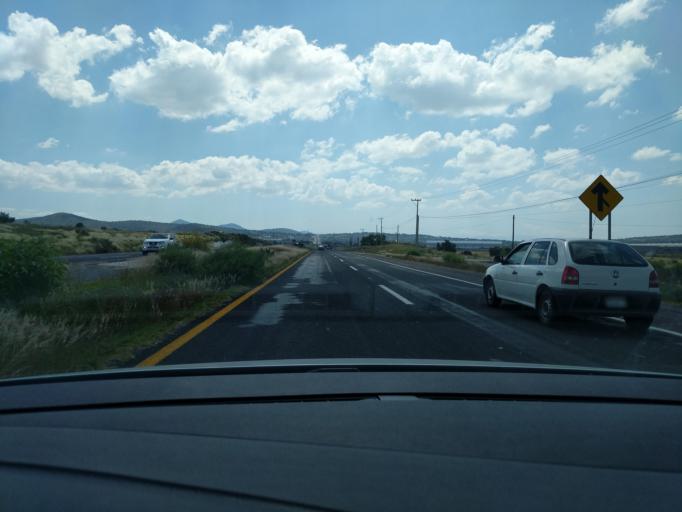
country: MX
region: Hidalgo
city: Zempoala
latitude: 19.9511
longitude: -98.6912
